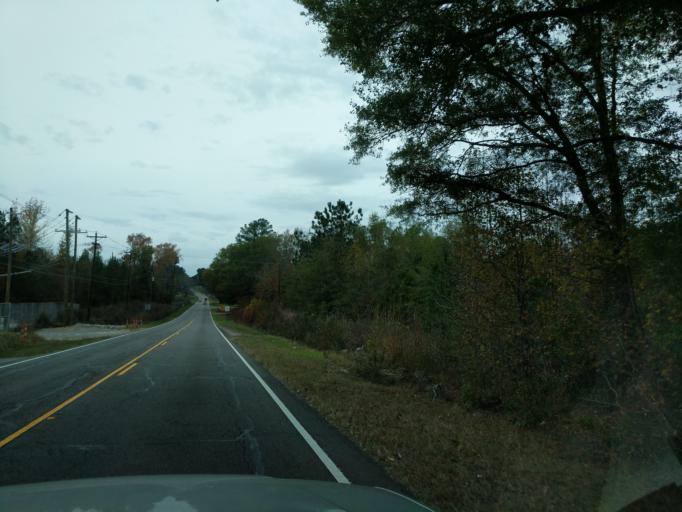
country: US
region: South Carolina
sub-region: Lexington County
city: Batesburg
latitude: 33.9139
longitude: -81.5638
